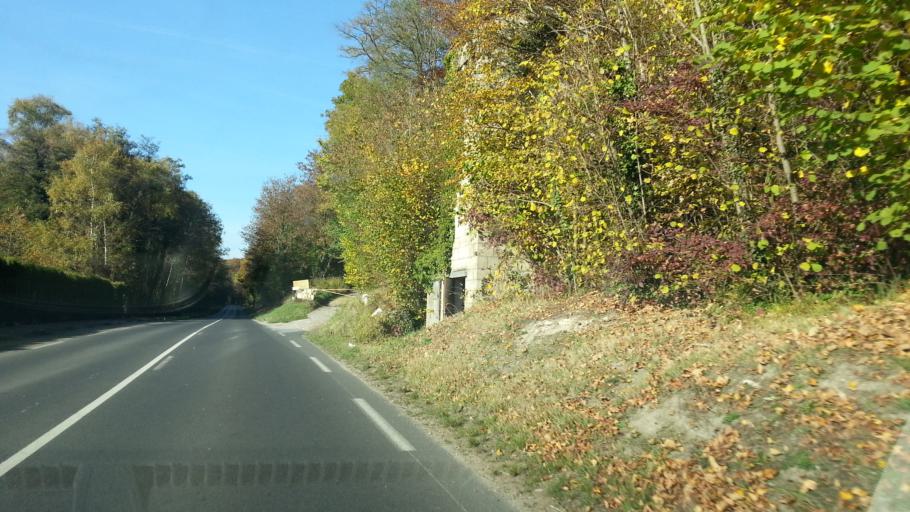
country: FR
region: Picardie
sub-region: Departement de l'Oise
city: Thiverny
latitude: 49.2621
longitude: 2.4067
